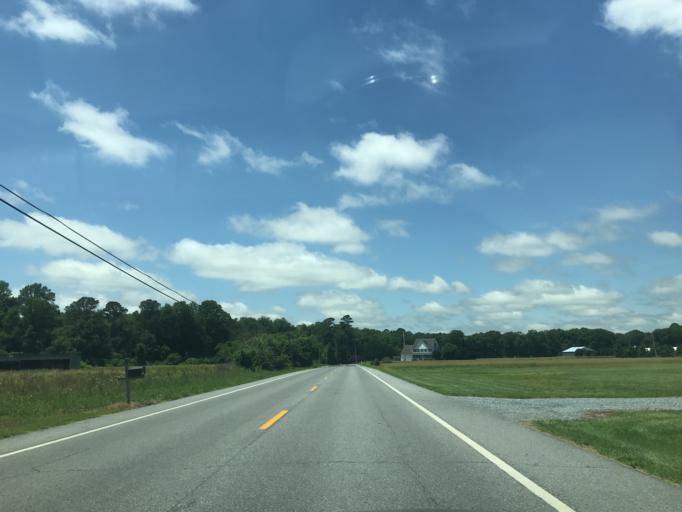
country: US
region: Maryland
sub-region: Caroline County
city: Federalsburg
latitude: 38.6983
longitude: -75.7398
